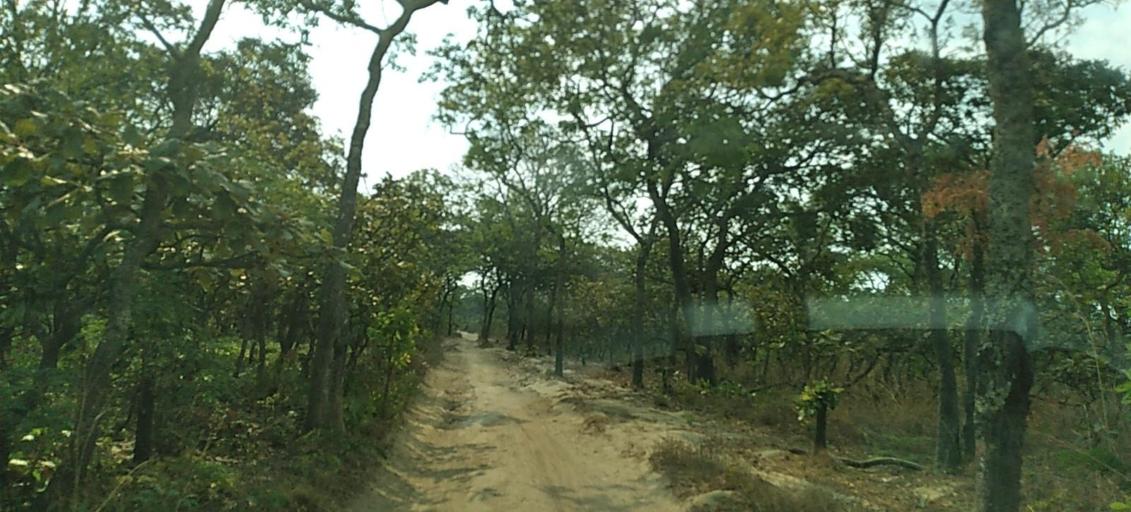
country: ZM
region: North-Western
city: Solwezi
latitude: -12.0743
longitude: 26.2346
